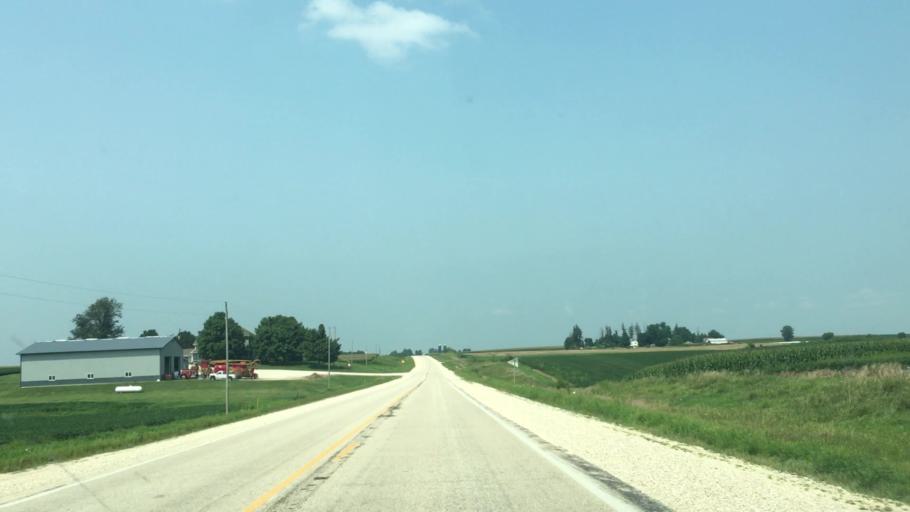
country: US
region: Iowa
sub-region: Fayette County
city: West Union
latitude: 42.9899
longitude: -91.8240
